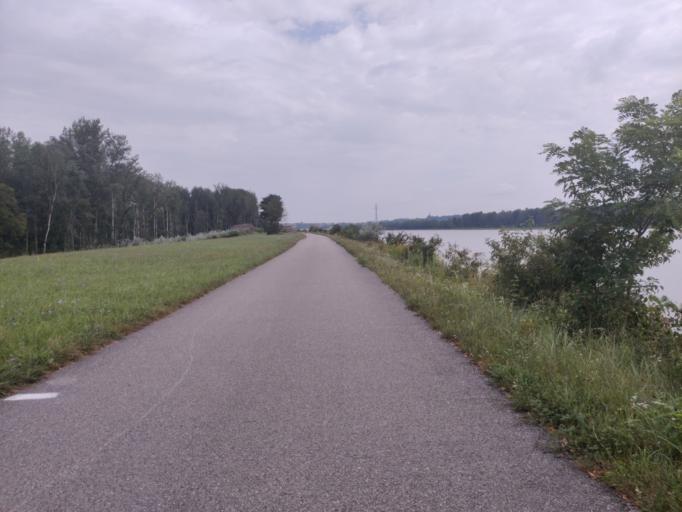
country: AT
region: Lower Austria
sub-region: Politischer Bezirk Amstetten
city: Strengberg
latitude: 48.1671
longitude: 14.6717
